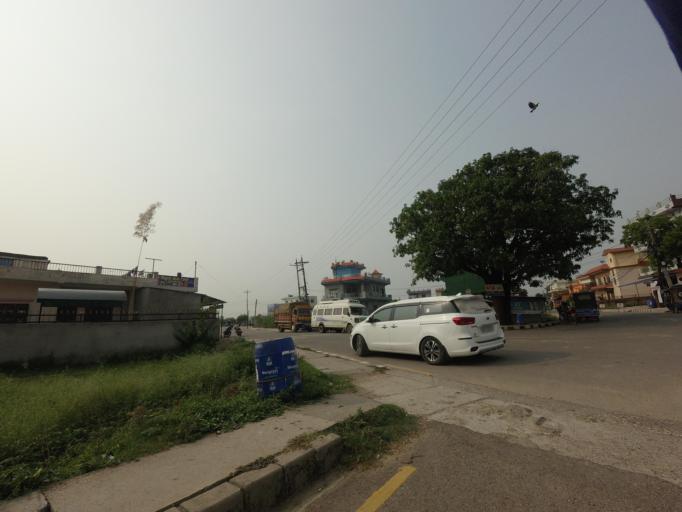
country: NP
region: Western Region
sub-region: Lumbini Zone
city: Bhairahawa
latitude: 27.5255
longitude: 83.4589
